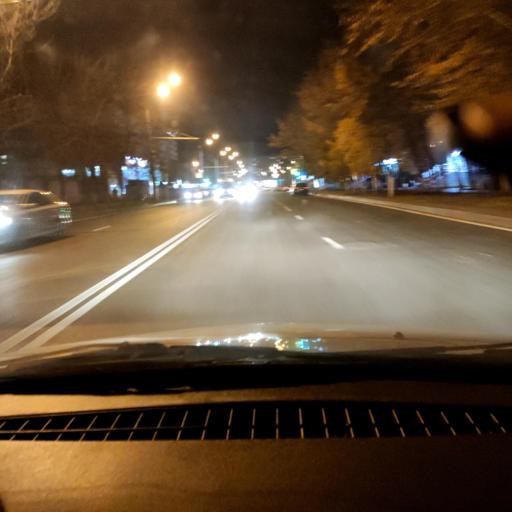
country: RU
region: Bashkortostan
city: Ufa
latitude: 54.6950
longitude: 55.9988
